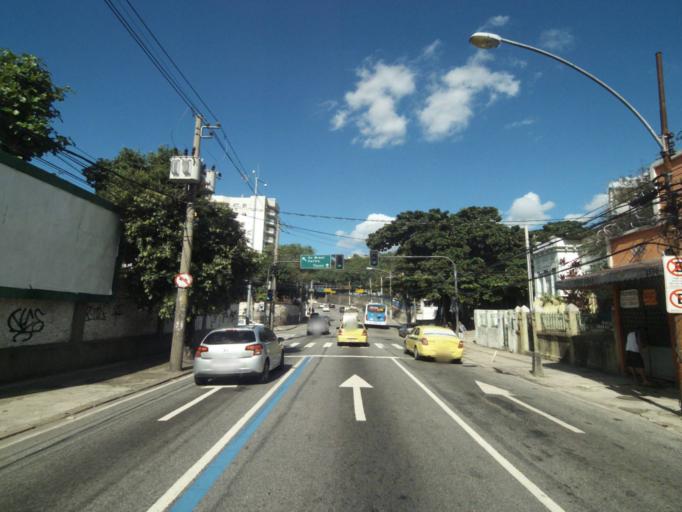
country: BR
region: Rio de Janeiro
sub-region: Rio De Janeiro
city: Rio de Janeiro
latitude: -22.9048
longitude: -43.2444
